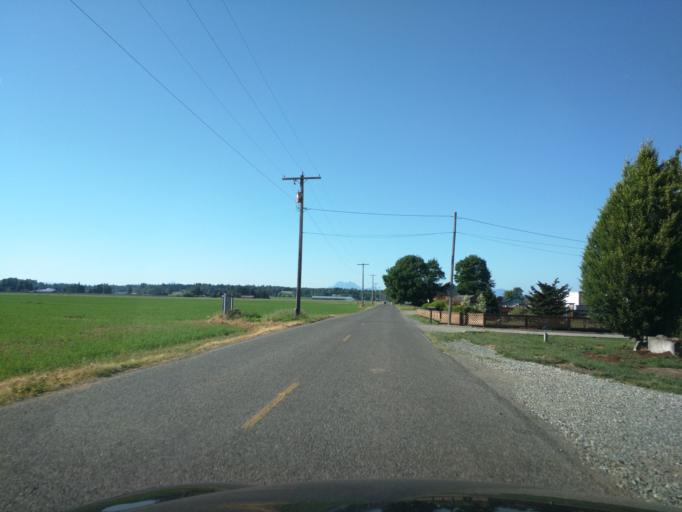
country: US
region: Washington
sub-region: Whatcom County
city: Lynden
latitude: 48.9844
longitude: -122.4518
